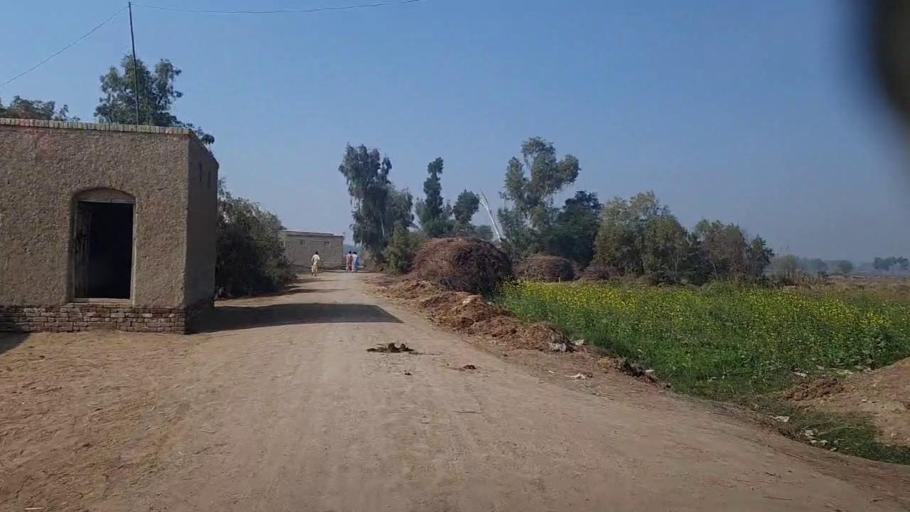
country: PK
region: Sindh
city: Khairpur
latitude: 27.9654
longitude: 69.6631
